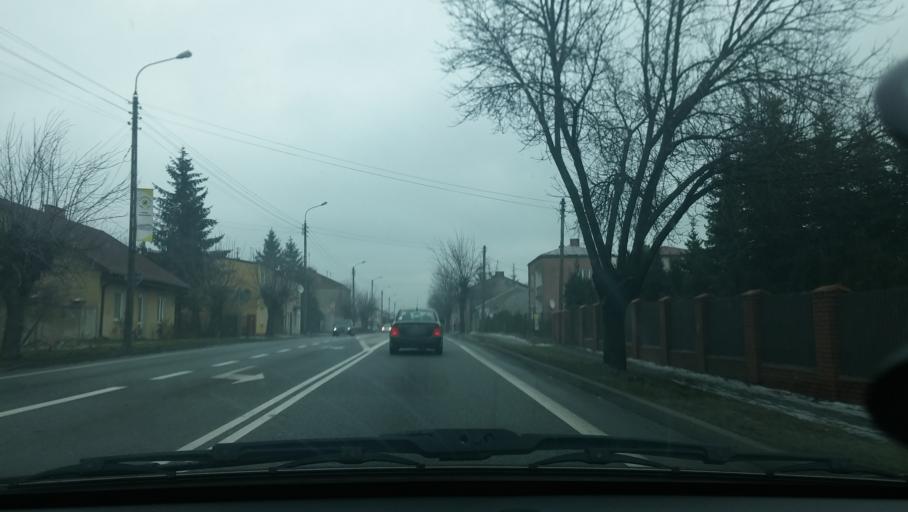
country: PL
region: Masovian Voivodeship
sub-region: Powiat minski
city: Kaluszyn
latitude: 52.2049
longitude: 21.8045
